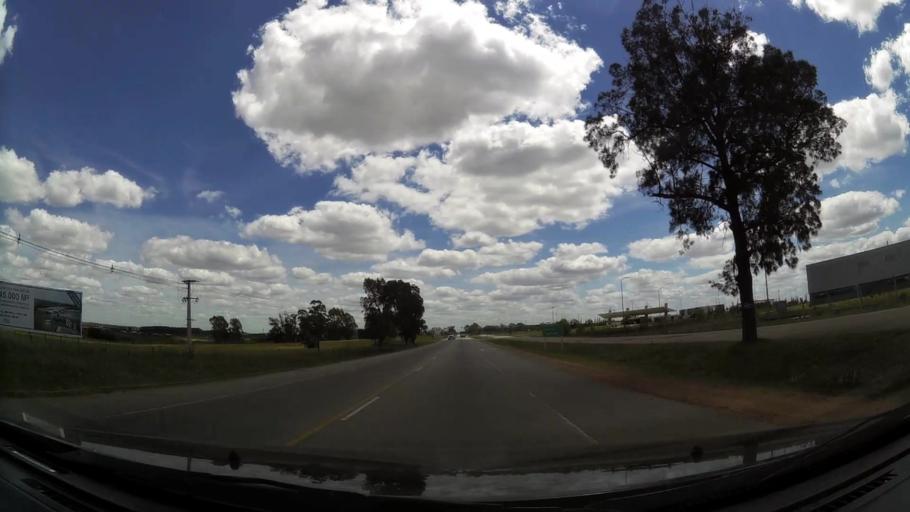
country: UY
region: Canelones
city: Colonia Nicolich
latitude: -34.8148
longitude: -56.0073
